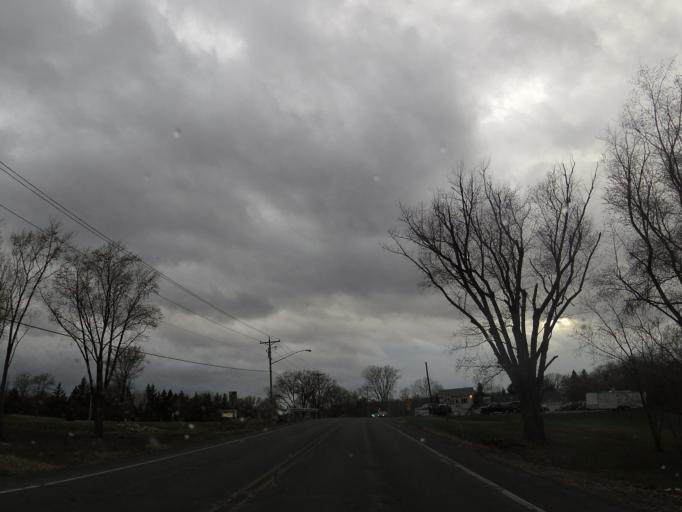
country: US
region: Wisconsin
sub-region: Saint Croix County
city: North Hudson
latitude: 45.0219
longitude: -92.6640
